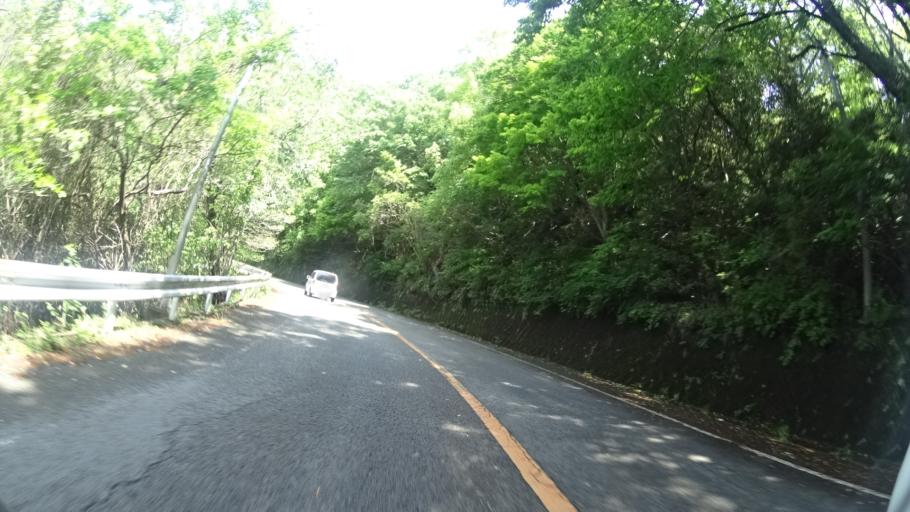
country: JP
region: Tokushima
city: Tokushima-shi
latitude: 34.0640
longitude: 134.5402
